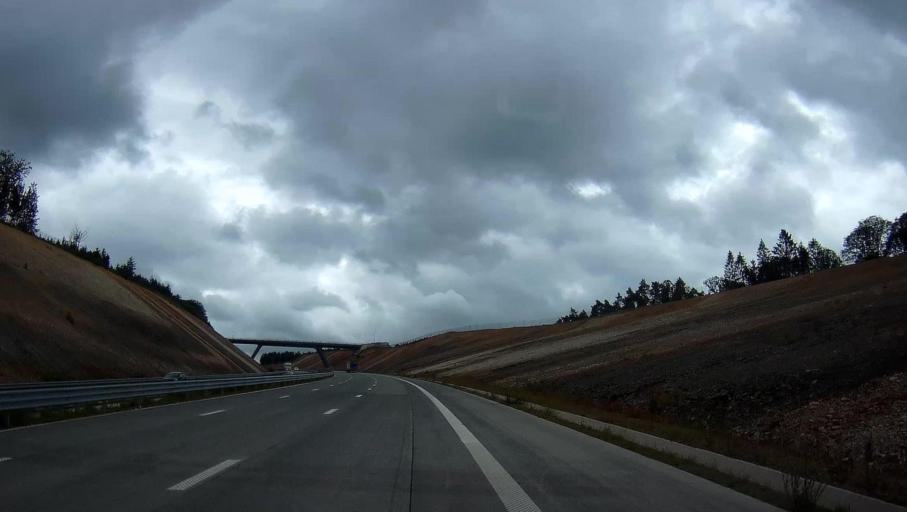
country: BE
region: Wallonia
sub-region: Province de Namur
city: Couvin
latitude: 50.0311
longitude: 4.5096
